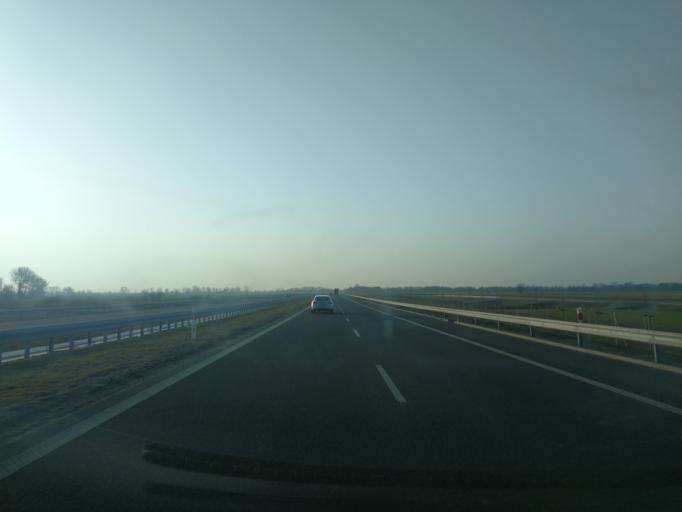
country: PL
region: Warmian-Masurian Voivodeship
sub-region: Powiat elblaski
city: Gronowo Elblaskie
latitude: 54.1685
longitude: 19.2303
